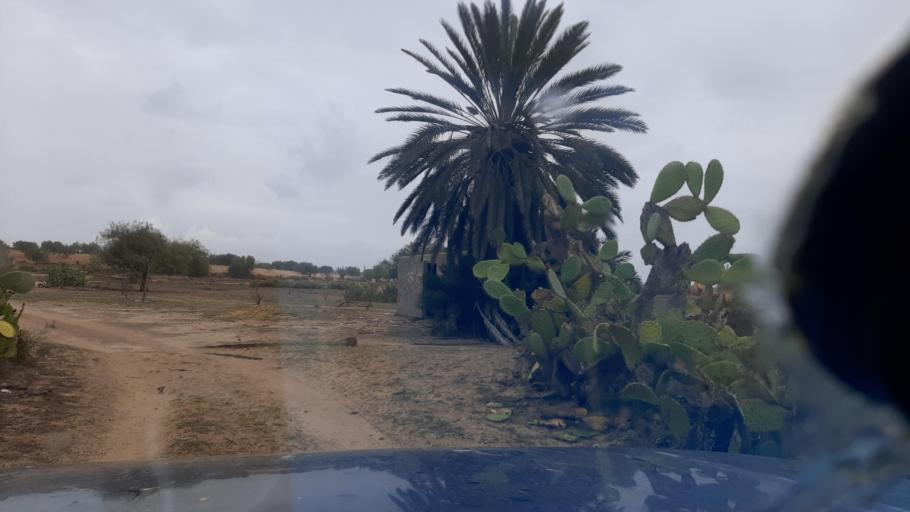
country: TN
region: Al Mahdiyah
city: Shurban
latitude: 35.4367
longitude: 10.4087
